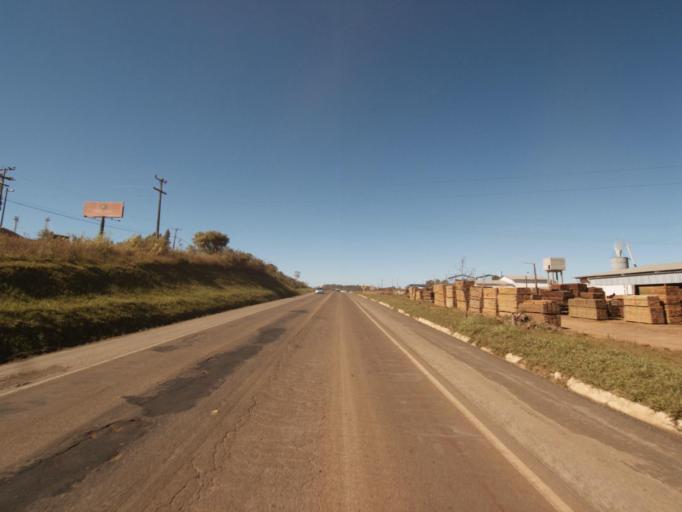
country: BR
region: Santa Catarina
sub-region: Sao Lourenco Do Oeste
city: Sao Lourenco dOeste
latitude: -26.7729
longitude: -53.2058
